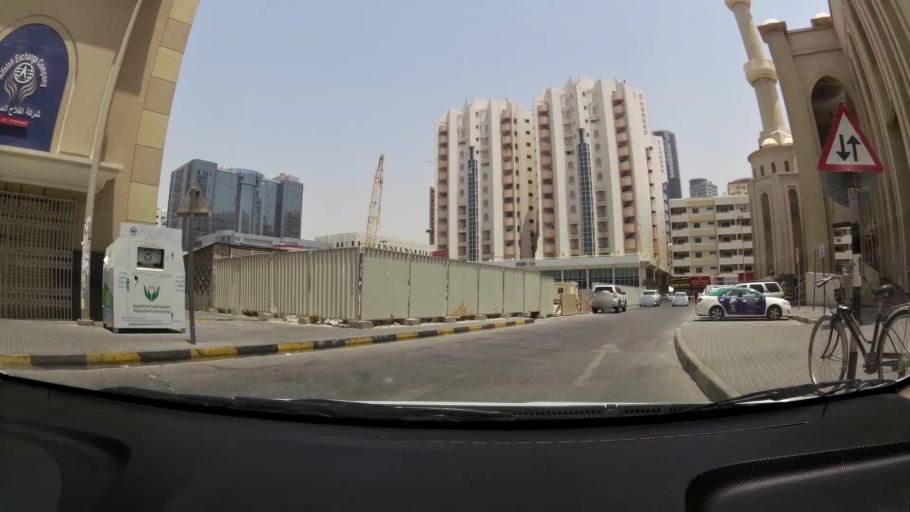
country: AE
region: Ash Shariqah
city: Sharjah
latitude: 25.3322
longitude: 55.3918
